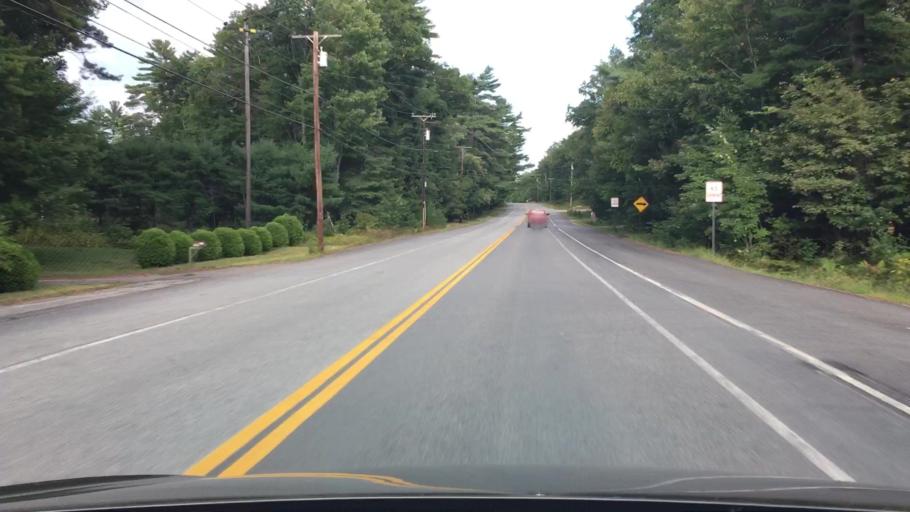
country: US
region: Maine
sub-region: Cumberland County
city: Bridgton
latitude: 44.0658
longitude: -70.8027
